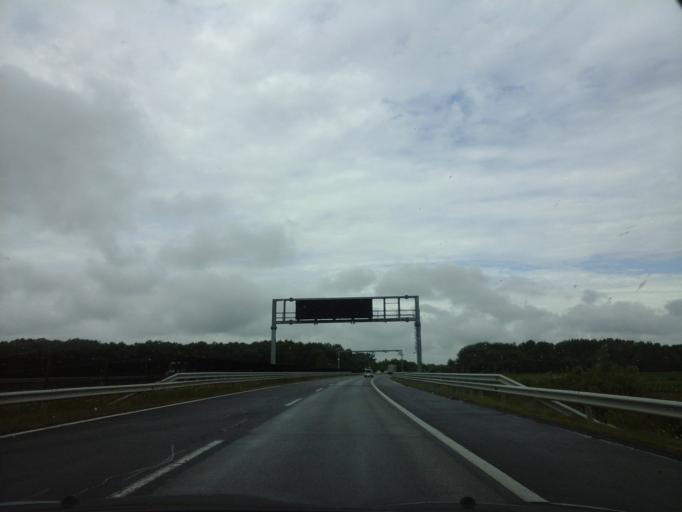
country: HU
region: Hajdu-Bihar
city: Polgar
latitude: 47.8482
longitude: 21.0700
